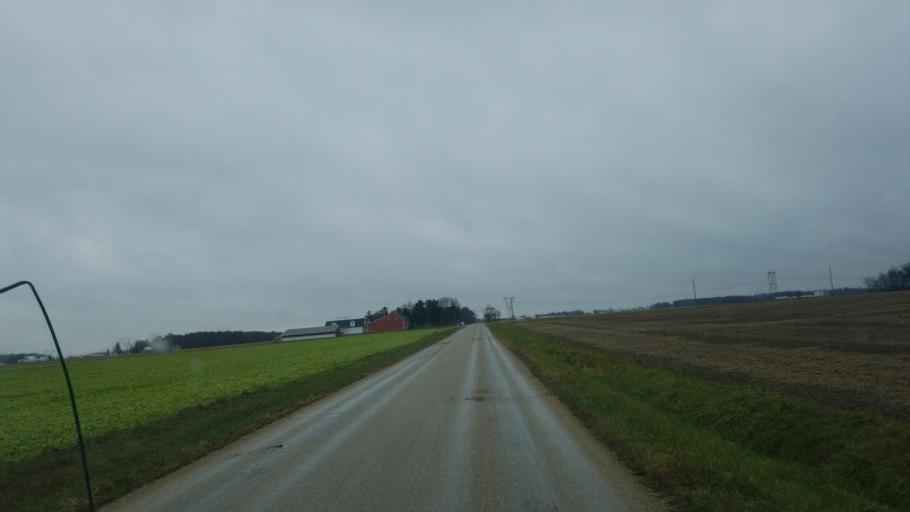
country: US
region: Indiana
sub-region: Adams County
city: Berne
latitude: 40.6898
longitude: -84.9173
